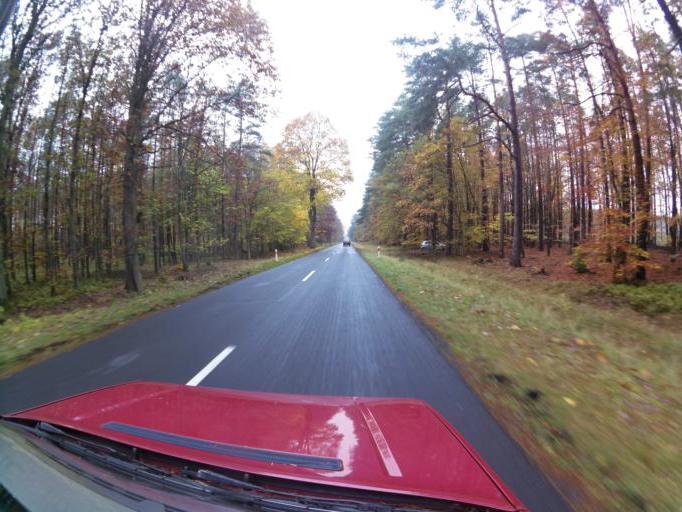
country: PL
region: West Pomeranian Voivodeship
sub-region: Powiat policki
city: Dobra
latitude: 53.5743
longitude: 14.4318
